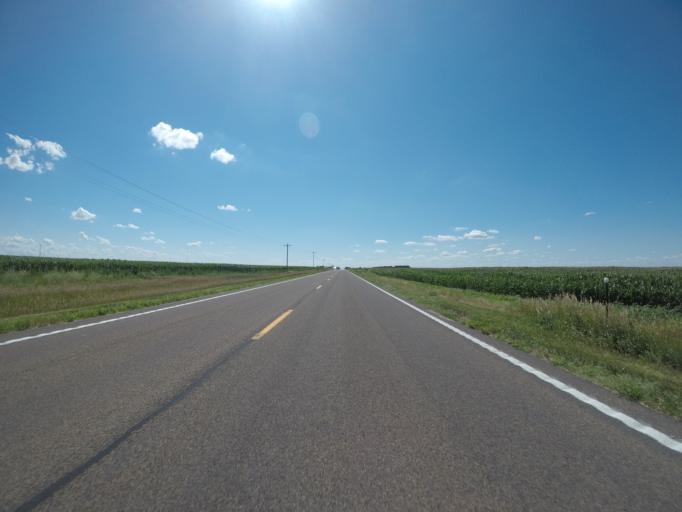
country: US
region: Nebraska
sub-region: Chase County
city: Imperial
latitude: 40.5377
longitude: -101.6505
